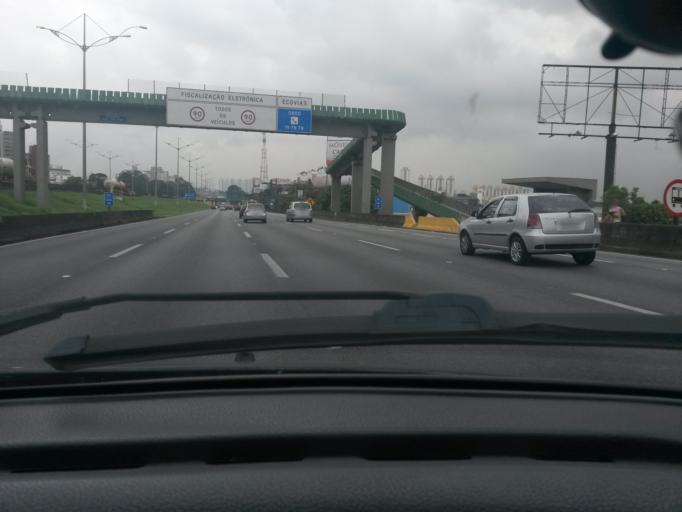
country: BR
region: Sao Paulo
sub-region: Sao Bernardo Do Campo
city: Sao Bernardo do Campo
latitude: -23.6843
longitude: -46.5670
